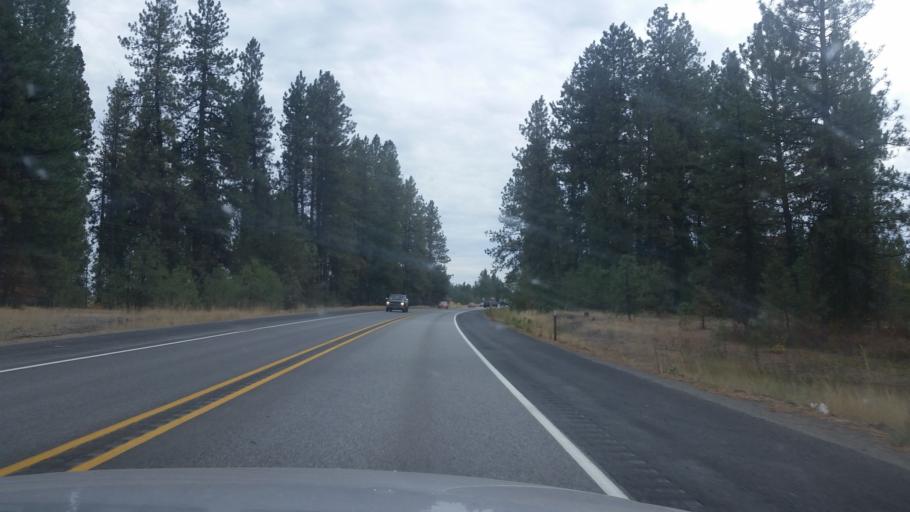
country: US
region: Washington
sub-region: Spokane County
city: Cheney
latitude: 47.5184
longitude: -117.5648
